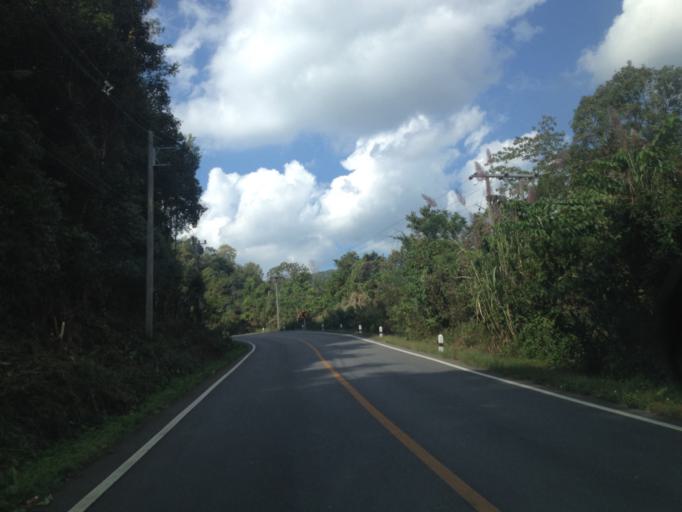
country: TH
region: Mae Hong Son
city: Ban Huai I Huak
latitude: 18.1479
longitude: 98.1477
